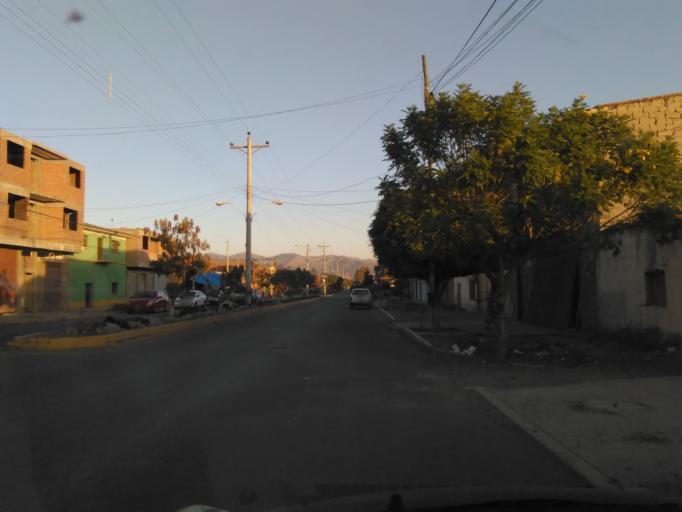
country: BO
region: Cochabamba
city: Punata
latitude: -17.5531
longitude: -65.8349
